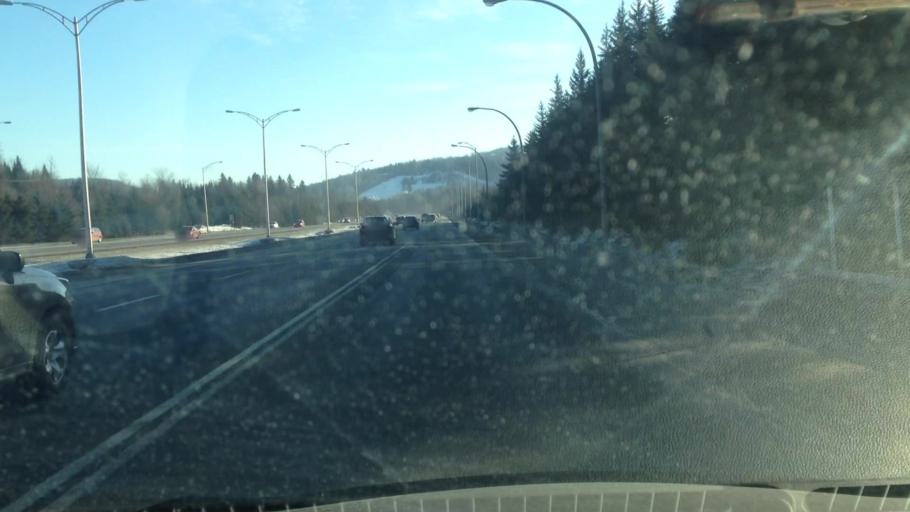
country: CA
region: Quebec
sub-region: Laurentides
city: Saint-Sauveur
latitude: 45.8891
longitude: -74.1414
